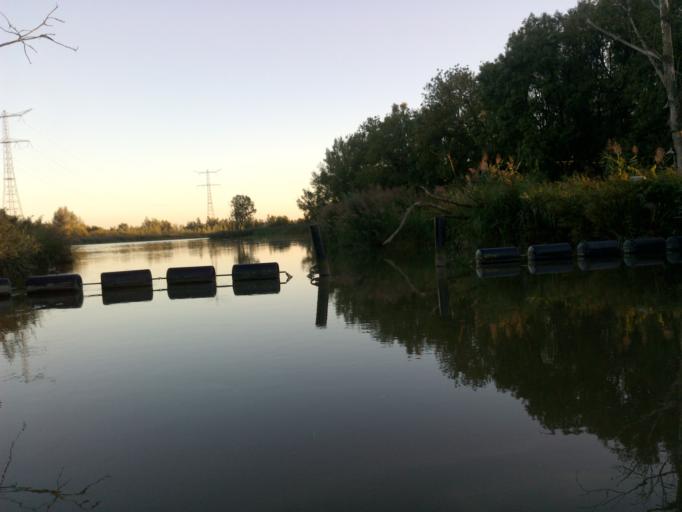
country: NL
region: South Holland
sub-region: Gemeente Sliedrecht
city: Sliedrecht
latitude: 51.8090
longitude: 4.7988
